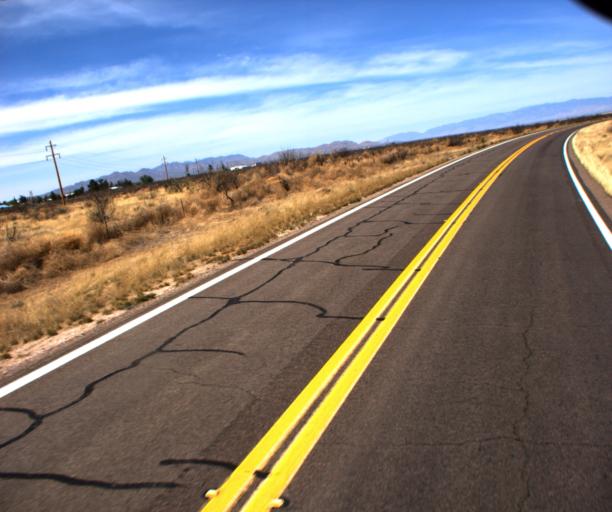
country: US
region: Arizona
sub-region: Cochise County
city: Willcox
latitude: 32.1077
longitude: -109.9141
